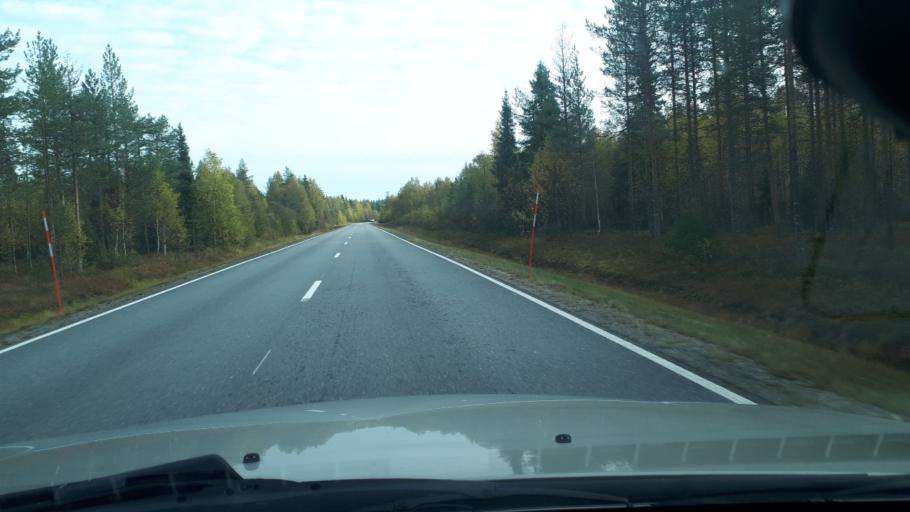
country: FI
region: Northern Ostrobothnia
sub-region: Oulu
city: Yli-Ii
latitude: 65.9223
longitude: 25.8050
